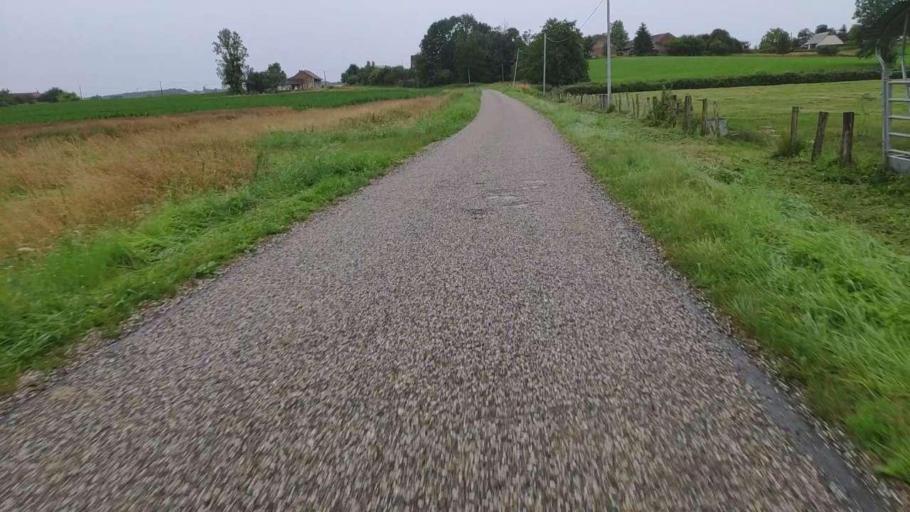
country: FR
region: Franche-Comte
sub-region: Departement du Jura
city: Chaussin
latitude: 46.8739
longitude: 5.4164
